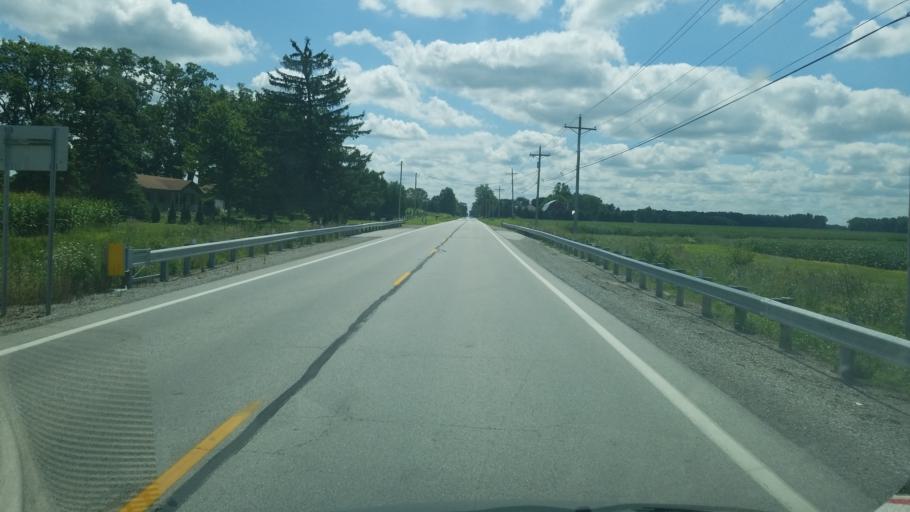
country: US
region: Ohio
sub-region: Henry County
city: Liberty Center
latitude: 41.5075
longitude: -84.0087
